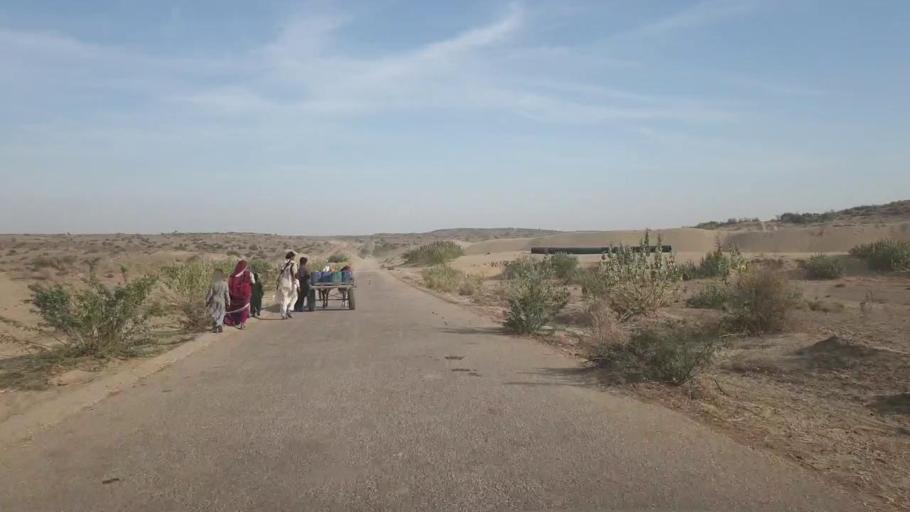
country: PK
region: Sindh
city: Nabisar
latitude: 25.0642
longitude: 69.6538
